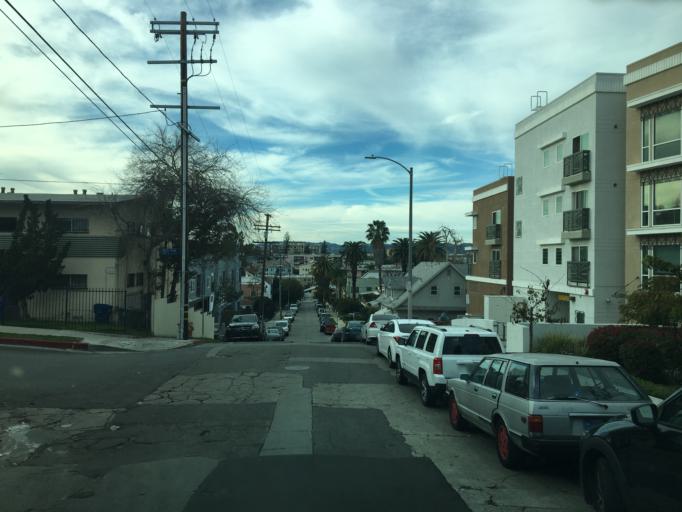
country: US
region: California
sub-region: Los Angeles County
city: Echo Park
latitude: 34.0639
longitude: -118.2765
